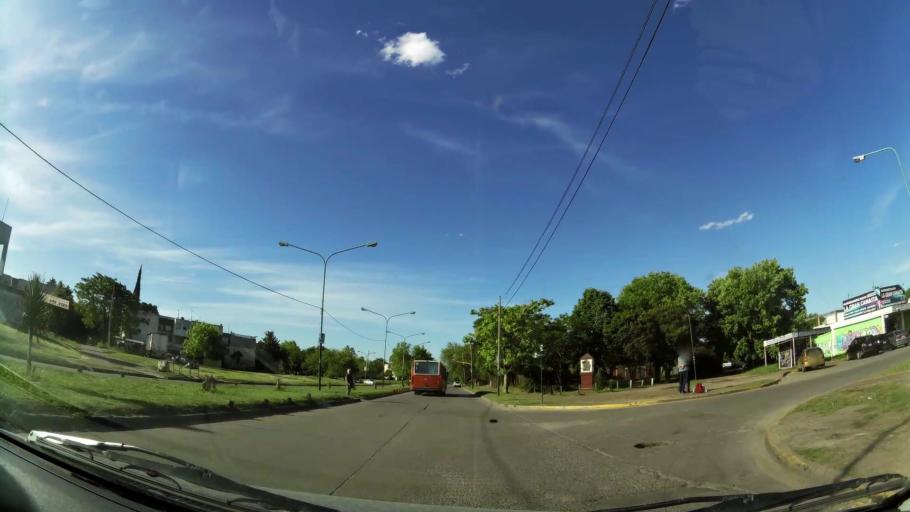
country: AR
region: Buenos Aires
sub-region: Partido de Almirante Brown
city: Adrogue
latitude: -34.8119
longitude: -58.3349
